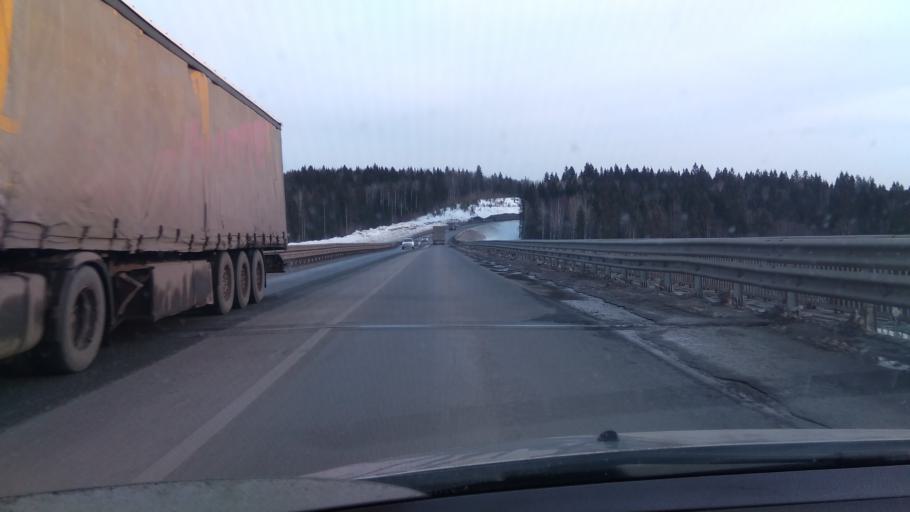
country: RU
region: Perm
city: Ferma
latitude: 57.9797
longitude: 56.3946
